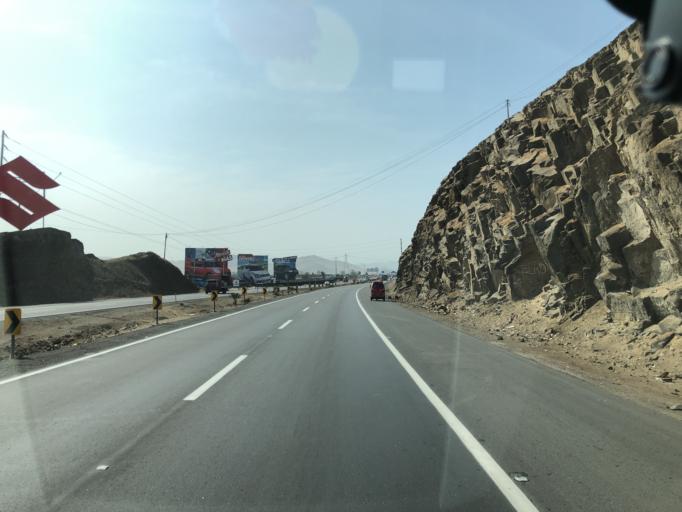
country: PE
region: Lima
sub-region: Provincia de Canete
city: Chilca
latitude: -12.5230
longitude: -76.7261
